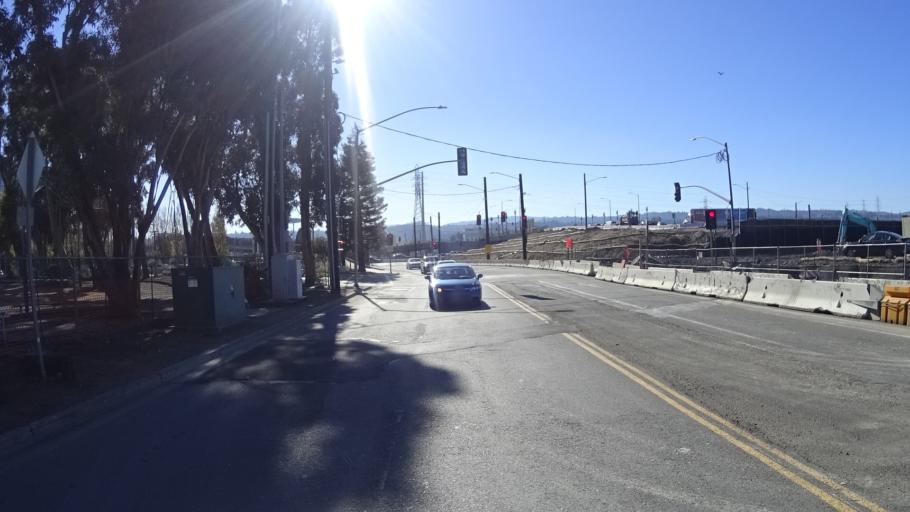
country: US
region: California
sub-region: San Mateo County
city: Burlingame
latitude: 37.5914
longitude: -122.3601
